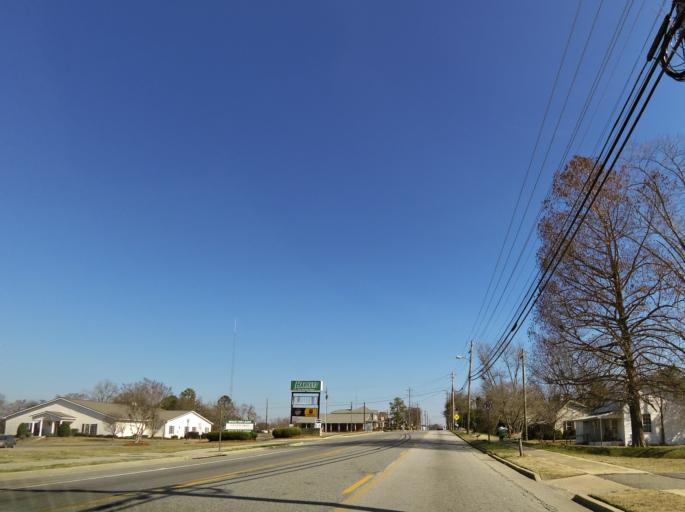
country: US
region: Georgia
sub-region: Bleckley County
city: Cochran
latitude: 32.3839
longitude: -83.3578
